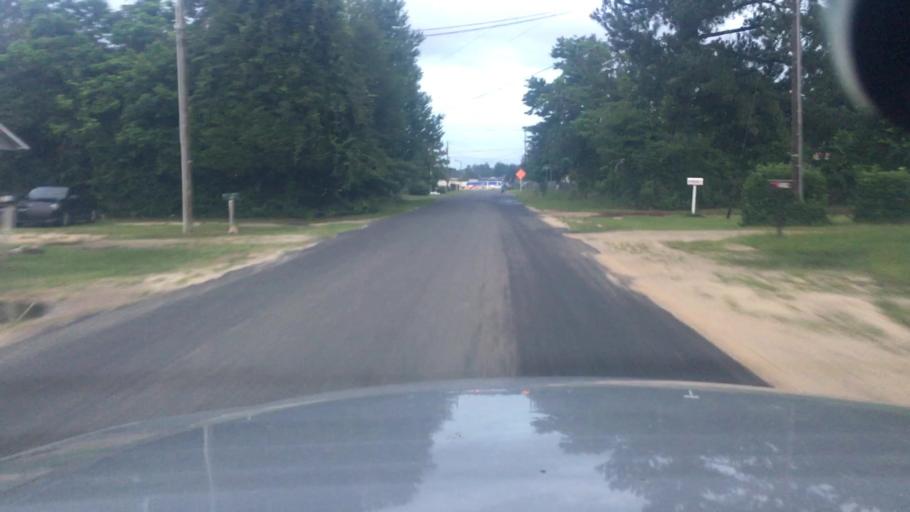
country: US
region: North Carolina
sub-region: Cumberland County
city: Hope Mills
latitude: 34.9835
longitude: -78.9098
